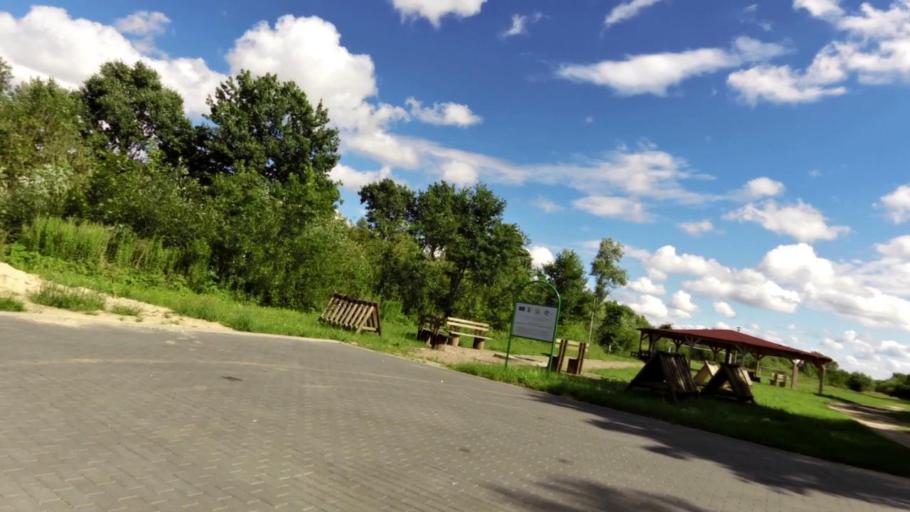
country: PL
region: West Pomeranian Voivodeship
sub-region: Powiat slawienski
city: Slawno
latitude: 54.4863
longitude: 16.7088
